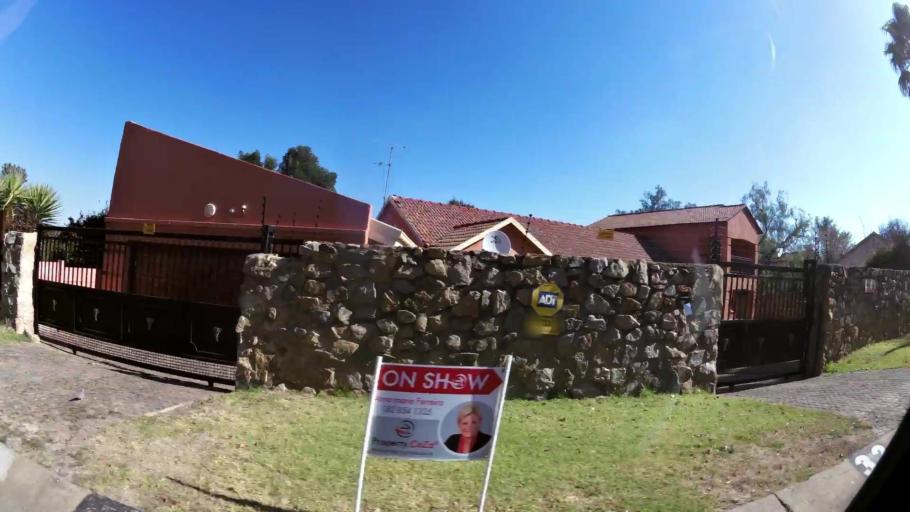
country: ZA
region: Gauteng
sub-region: City of Johannesburg Metropolitan Municipality
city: Roodepoort
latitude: -26.1157
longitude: 27.9267
